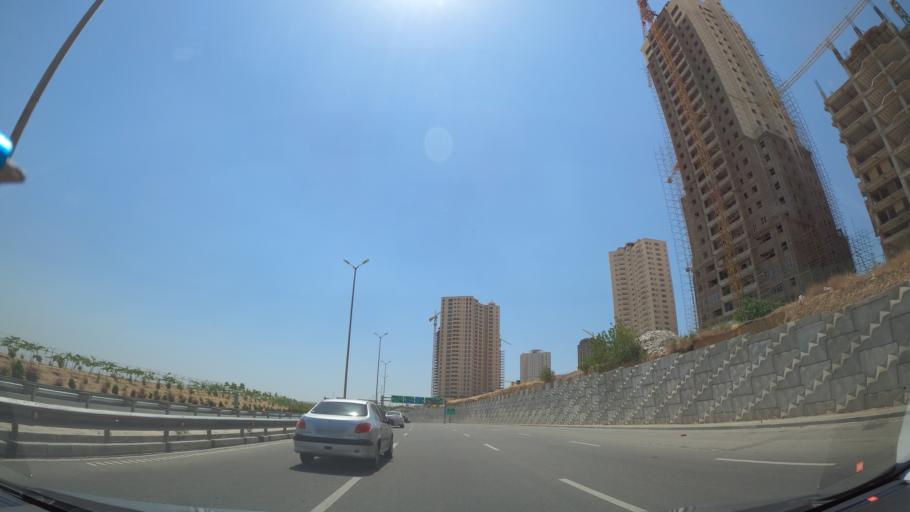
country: IR
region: Tehran
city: Shahr-e Qods
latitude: 35.7517
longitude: 51.1386
